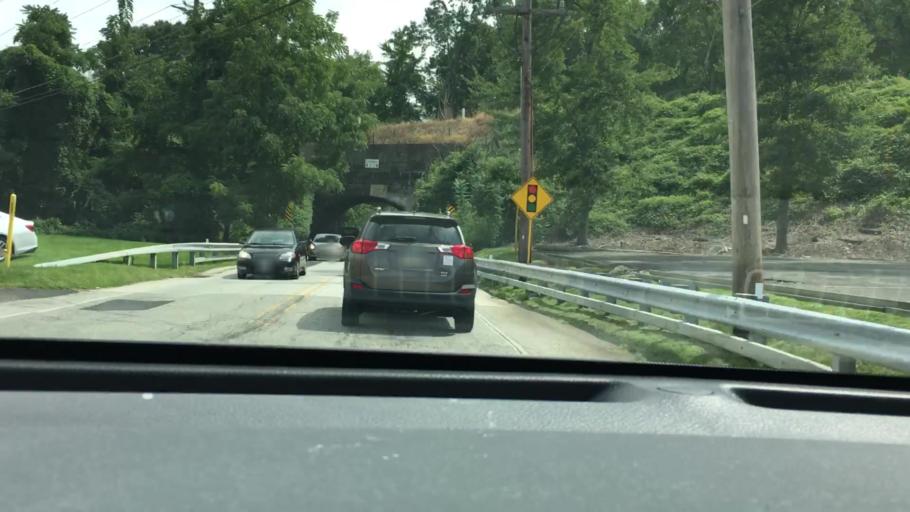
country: US
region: Pennsylvania
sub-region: Bucks County
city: Warminster Heights
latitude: 40.1609
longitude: -75.0782
